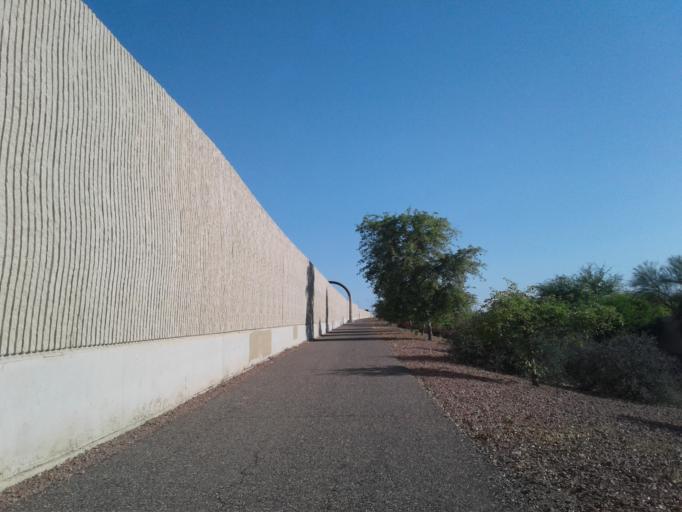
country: US
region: Arizona
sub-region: Maricopa County
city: Paradise Valley
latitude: 33.6592
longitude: -111.9995
